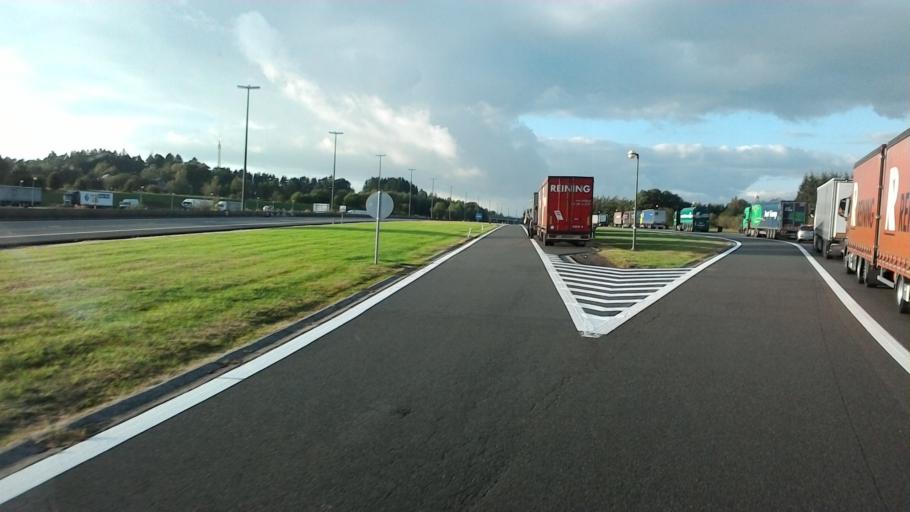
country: BE
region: Wallonia
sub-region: Province du Luxembourg
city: Manhay
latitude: 50.3587
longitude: 5.6757
